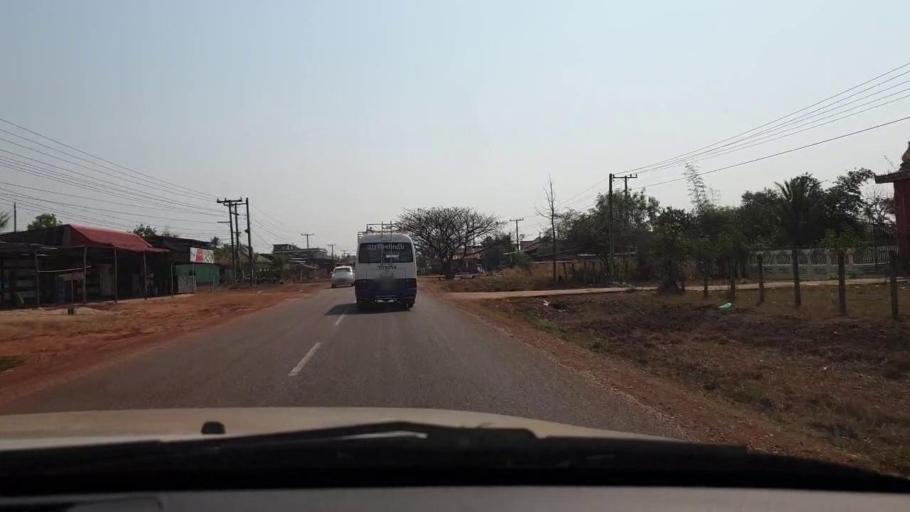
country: TH
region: Nong Khai
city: Nong Khai
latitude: 18.0544
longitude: 102.8363
